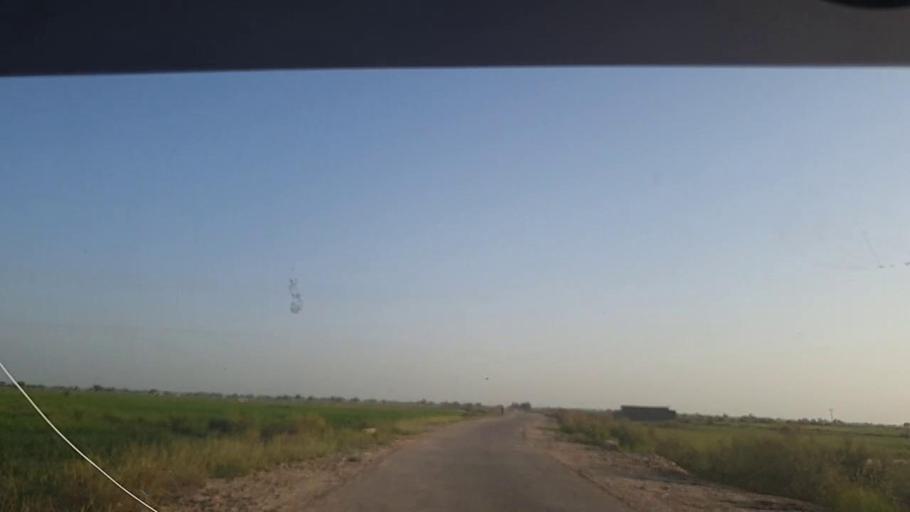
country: PK
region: Sindh
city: Thul
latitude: 28.1439
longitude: 68.8878
